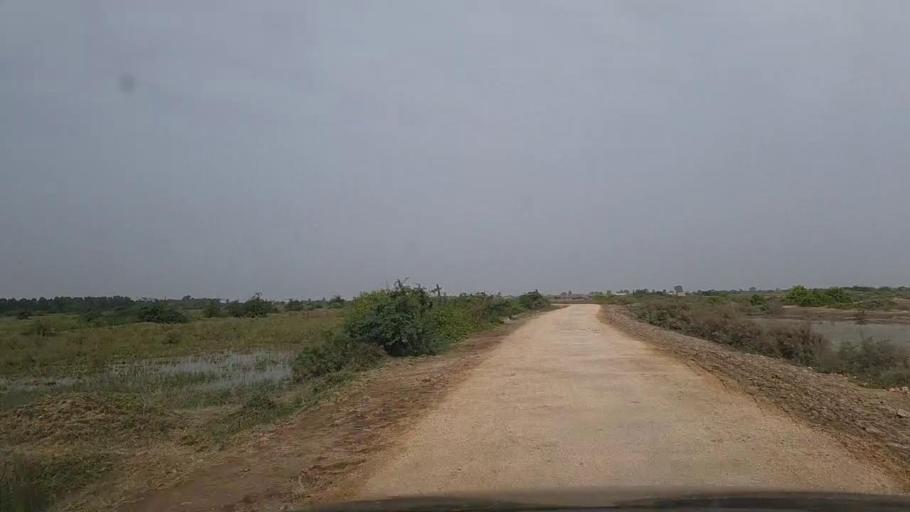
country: PK
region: Sindh
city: Thatta
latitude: 24.7437
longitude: 67.8265
